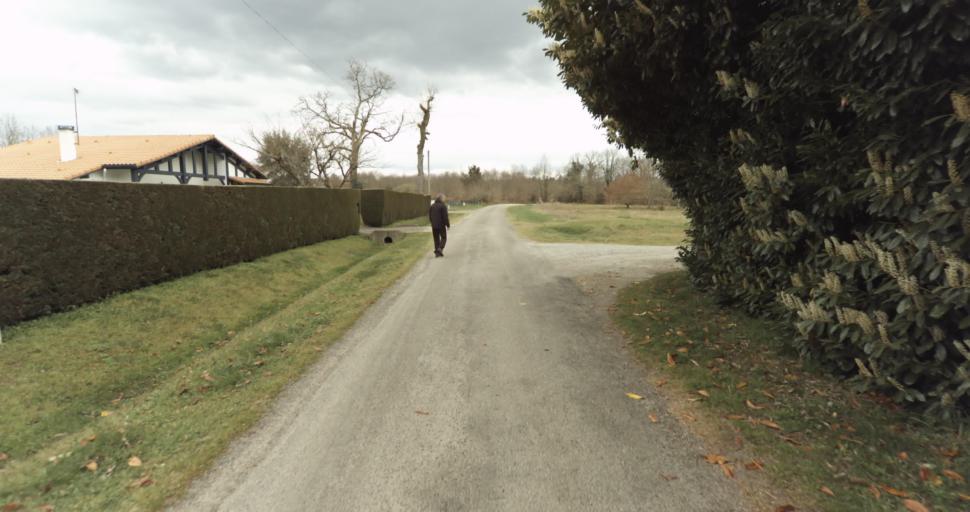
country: FR
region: Aquitaine
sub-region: Departement des Landes
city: Sarbazan
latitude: 44.0249
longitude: -0.3156
